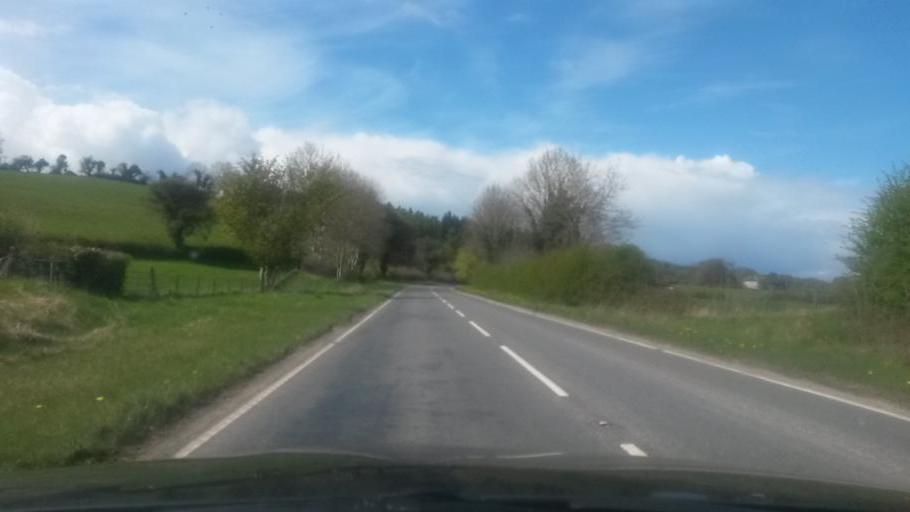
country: GB
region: Northern Ireland
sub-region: Fermanagh District
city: Enniskillen
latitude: 54.3684
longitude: -7.6812
